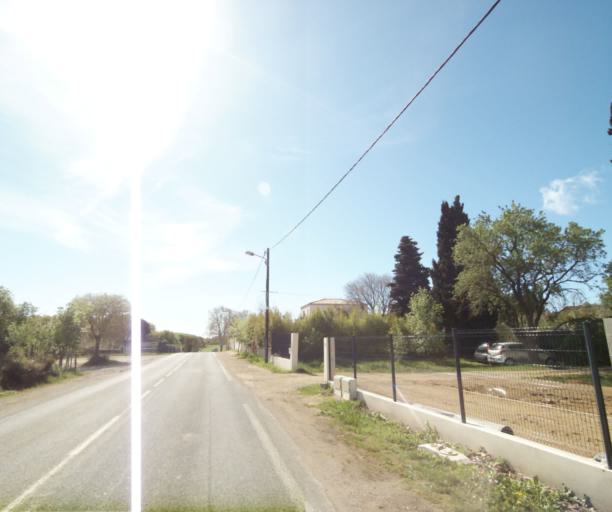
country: FR
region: Languedoc-Roussillon
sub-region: Departement de l'Herault
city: Villeneuve-les-Maguelone
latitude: 43.5541
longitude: 3.8451
